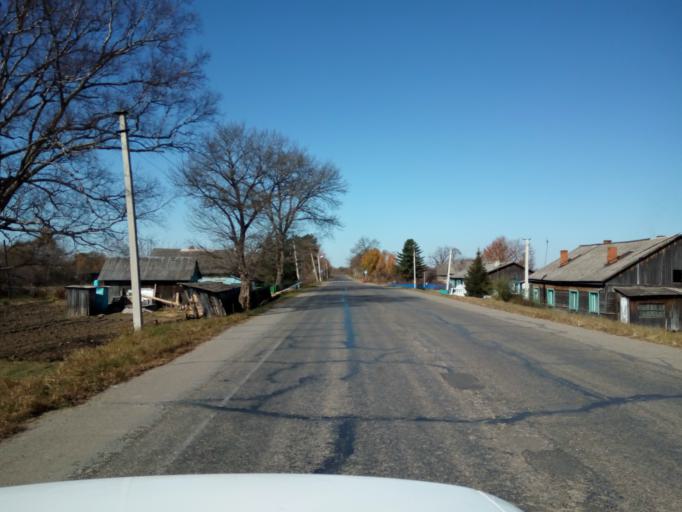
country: RU
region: Primorskiy
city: Dal'nerechensk
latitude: 45.9150
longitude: 133.7877
